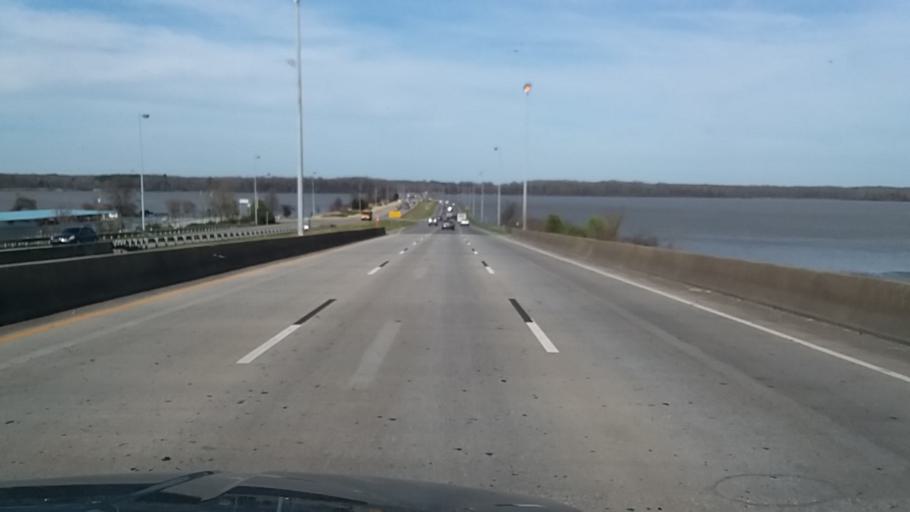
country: US
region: Alabama
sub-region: Morgan County
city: Decatur
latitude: 34.6147
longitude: -86.9708
